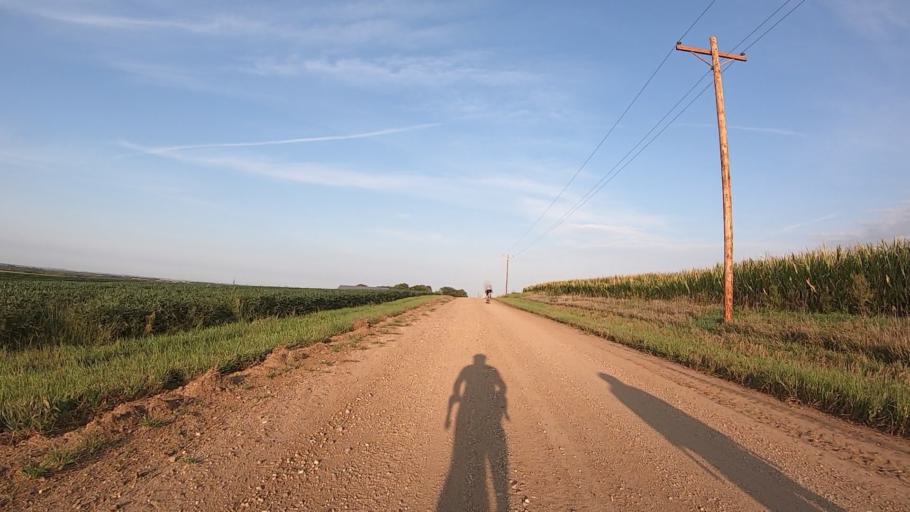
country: US
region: Kansas
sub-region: Marshall County
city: Marysville
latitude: 39.7694
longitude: -96.7430
